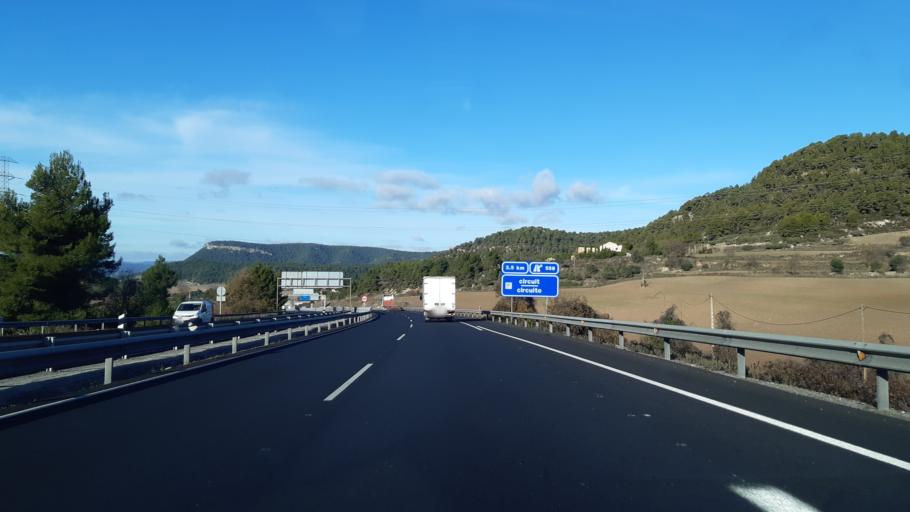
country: ES
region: Catalonia
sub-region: Provincia de Barcelona
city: Castelloli
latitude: 41.5961
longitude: 1.7190
